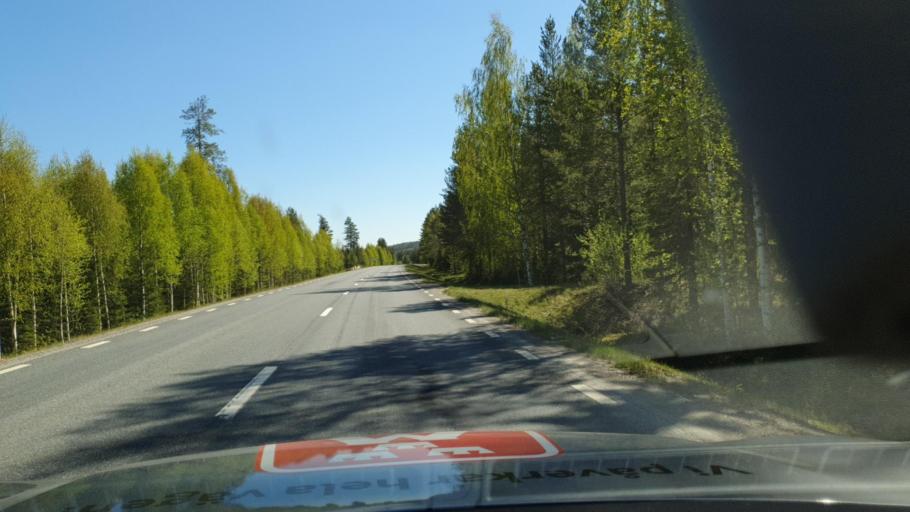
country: SE
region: Vaesternorrland
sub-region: OErnskoeldsviks Kommun
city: Ornskoldsvik
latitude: 63.6308
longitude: 18.5518
